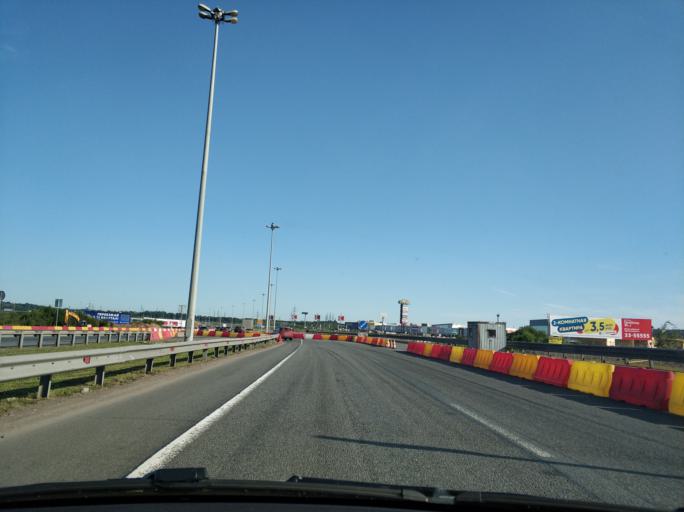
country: RU
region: Leningrad
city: Bugry
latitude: 60.0833
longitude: 30.3788
